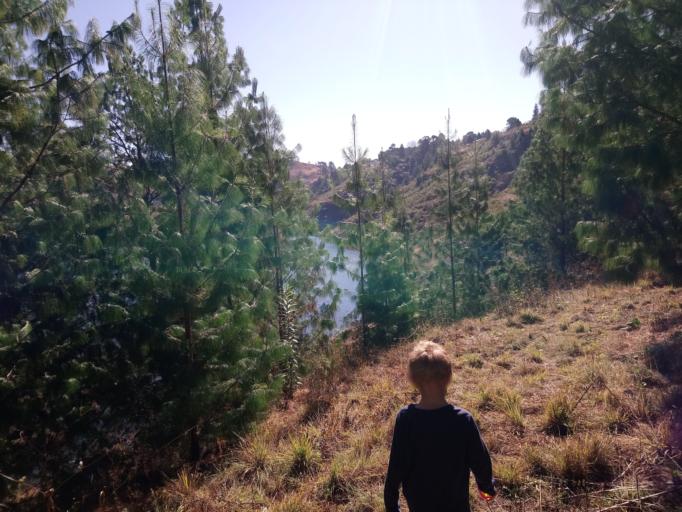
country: ZA
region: KwaZulu-Natal
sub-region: uMgungundlovu District Municipality
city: Mooirivier
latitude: -29.3342
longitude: 29.9181
